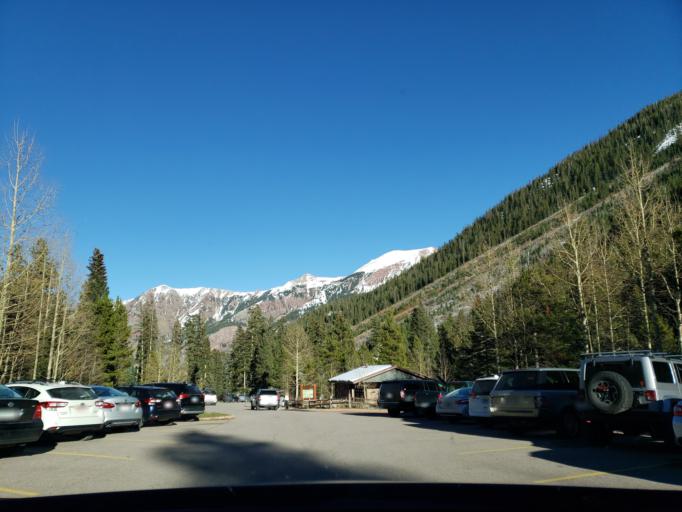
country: US
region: Colorado
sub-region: Pitkin County
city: Snowmass Village
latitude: 39.0987
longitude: -106.9401
